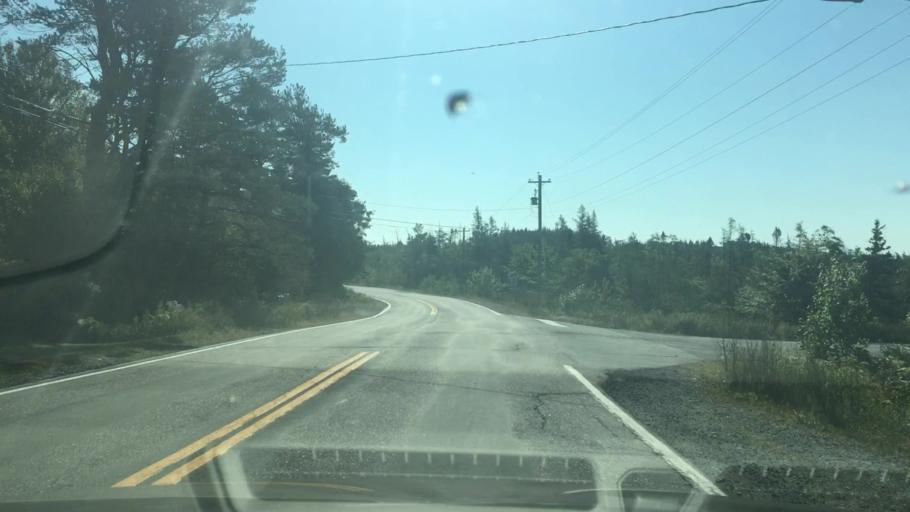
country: CA
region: Nova Scotia
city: Cole Harbour
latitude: 44.7759
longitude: -63.0556
